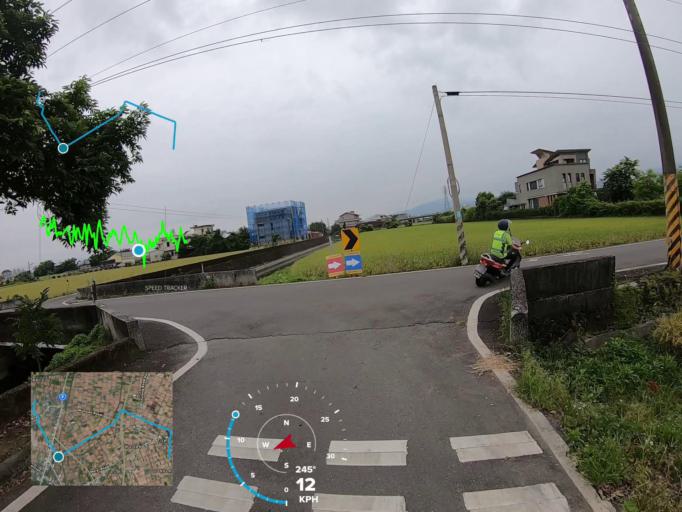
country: TW
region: Taiwan
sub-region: Yilan
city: Yilan
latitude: 24.7769
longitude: 121.7669
